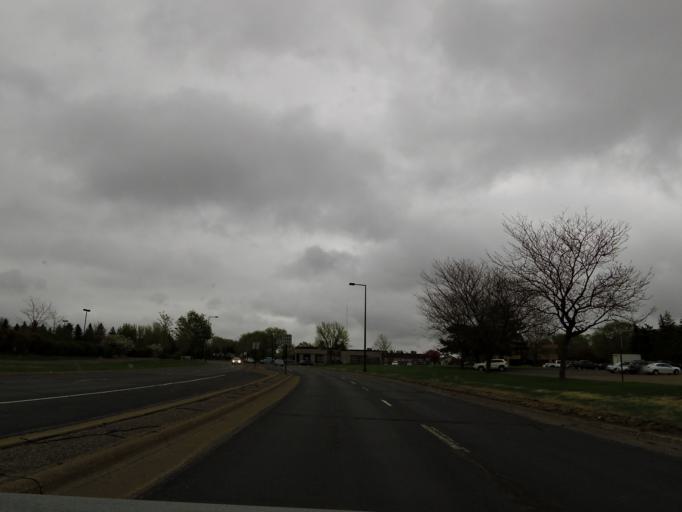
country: US
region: Minnesota
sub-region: Washington County
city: Stillwater
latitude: 45.0404
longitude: -92.8299
